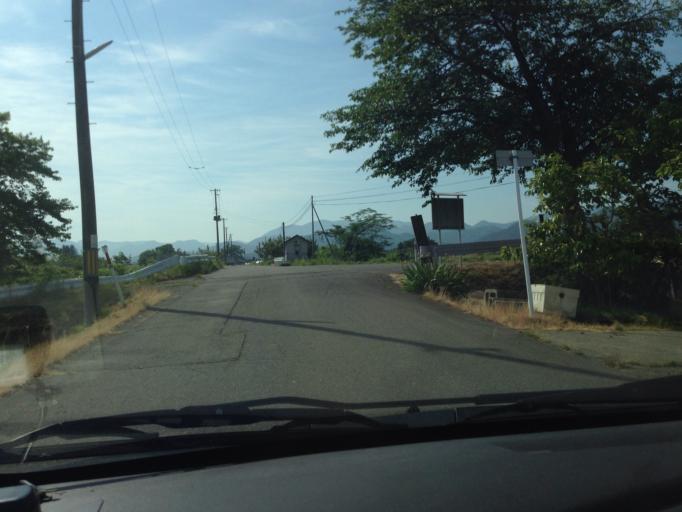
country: JP
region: Fukushima
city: Kitakata
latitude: 37.4511
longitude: 139.8244
